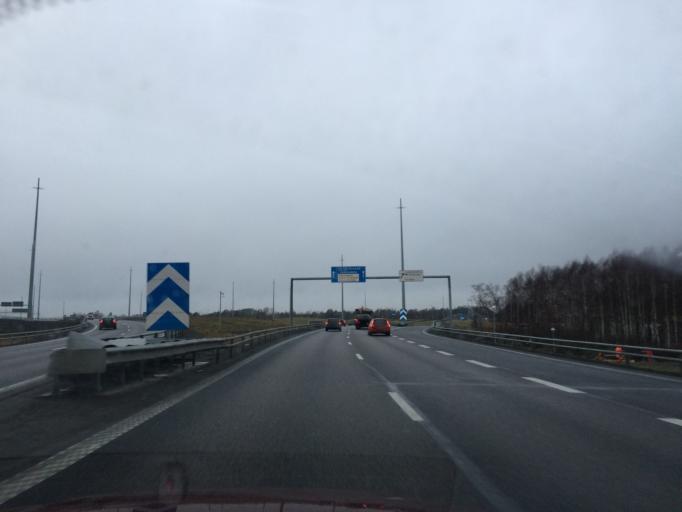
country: SE
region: Vaestra Goetaland
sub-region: Goteborg
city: Majorna
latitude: 57.7048
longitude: 11.8798
